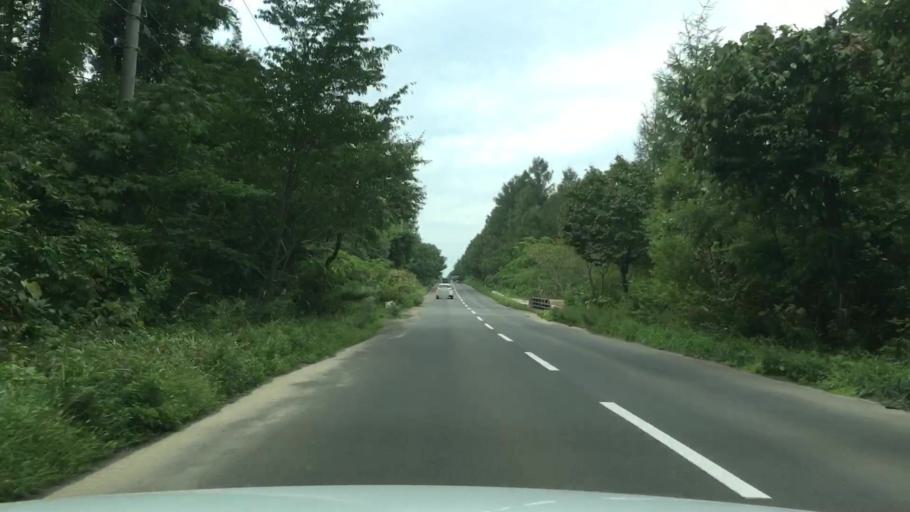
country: JP
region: Aomori
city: Shimokizukuri
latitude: 40.7114
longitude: 140.3302
